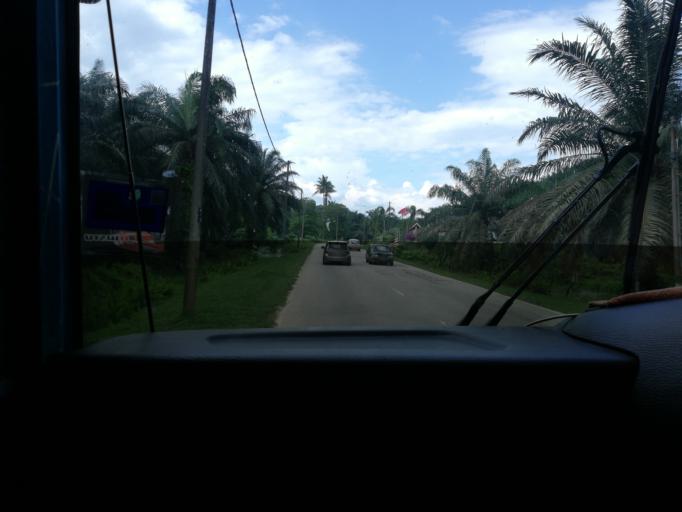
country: MY
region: Kedah
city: Kulim
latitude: 5.2642
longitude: 100.6074
